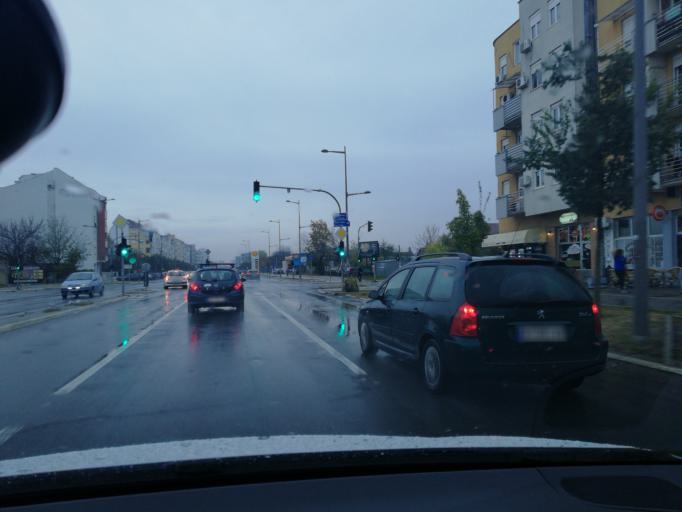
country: RS
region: Autonomna Pokrajina Vojvodina
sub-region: Juznobacki Okrug
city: Novi Sad
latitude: 45.2408
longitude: 19.8105
